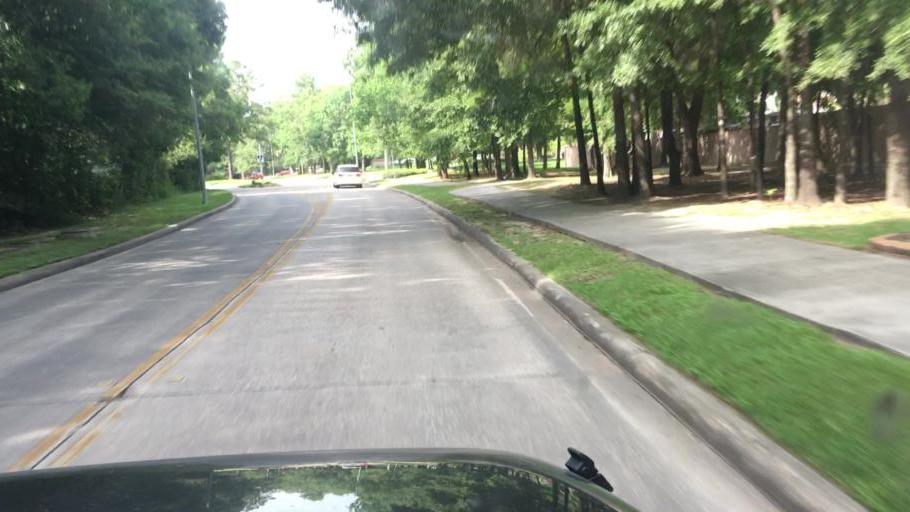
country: US
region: Texas
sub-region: Harris County
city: Atascocita
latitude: 30.0066
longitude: -95.1729
